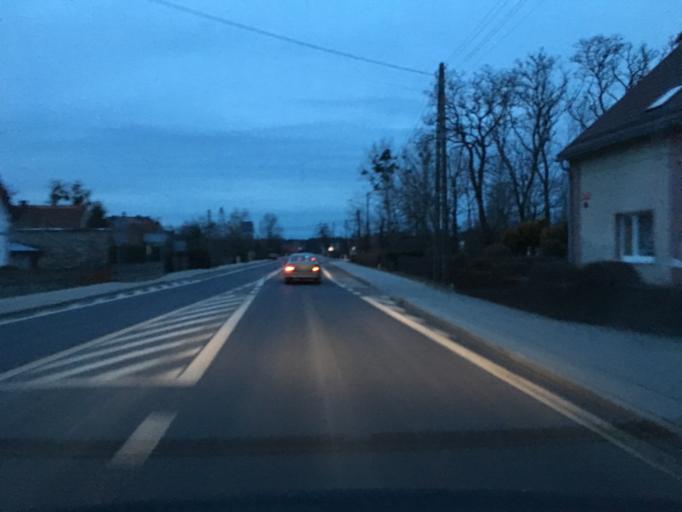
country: PL
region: Opole Voivodeship
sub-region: Powiat opolski
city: Dabrowa
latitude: 50.7220
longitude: 17.7609
